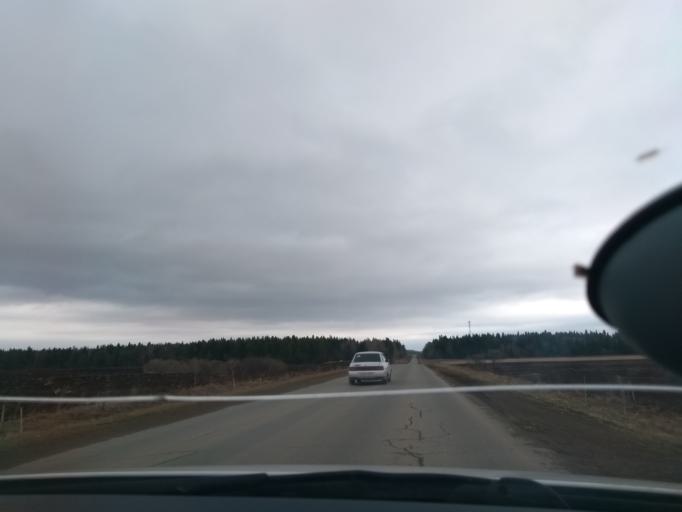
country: RU
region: Perm
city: Kungur
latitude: 57.3924
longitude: 56.8698
